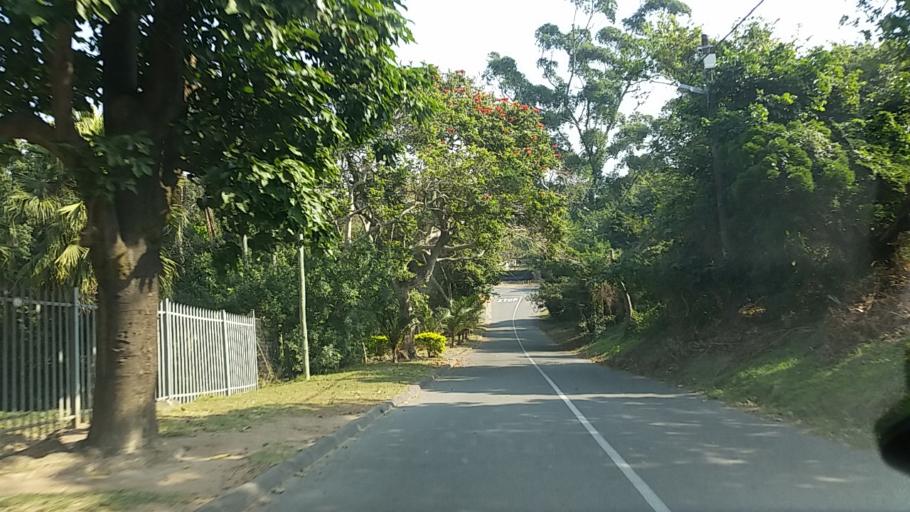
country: ZA
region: KwaZulu-Natal
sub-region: eThekwini Metropolitan Municipality
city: Berea
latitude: -29.8340
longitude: 30.9373
